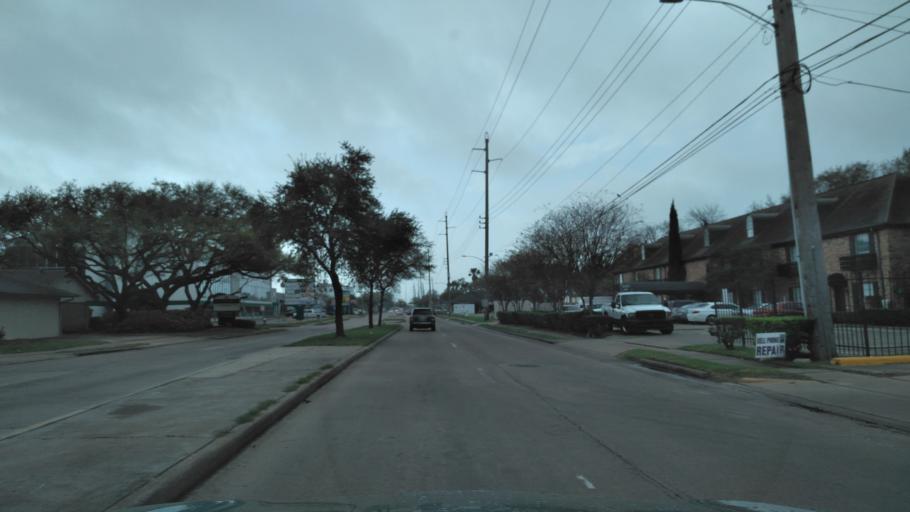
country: US
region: Texas
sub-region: Harris County
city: Hunters Creek Village
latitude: 29.7350
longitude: -95.4843
